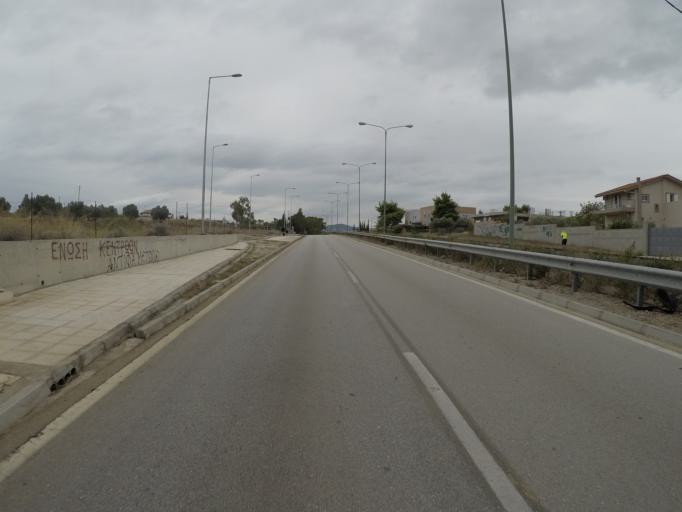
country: GR
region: Peloponnese
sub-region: Nomos Korinthias
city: Korinthos
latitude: 37.9435
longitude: 22.9792
